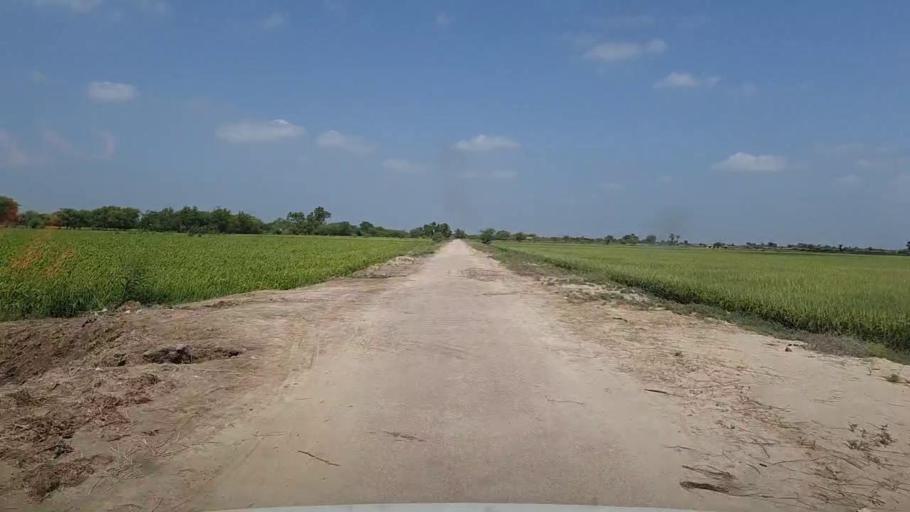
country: PK
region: Sindh
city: Kario
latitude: 24.6898
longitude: 68.5881
